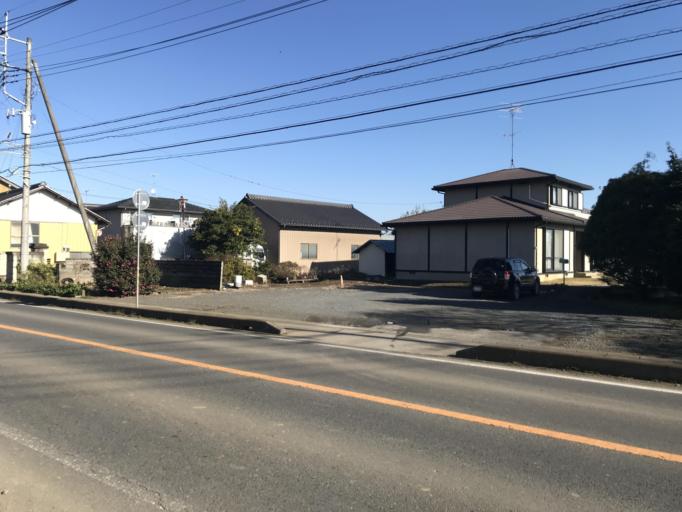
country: JP
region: Tochigi
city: Oyama
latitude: 36.2221
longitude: 139.8241
